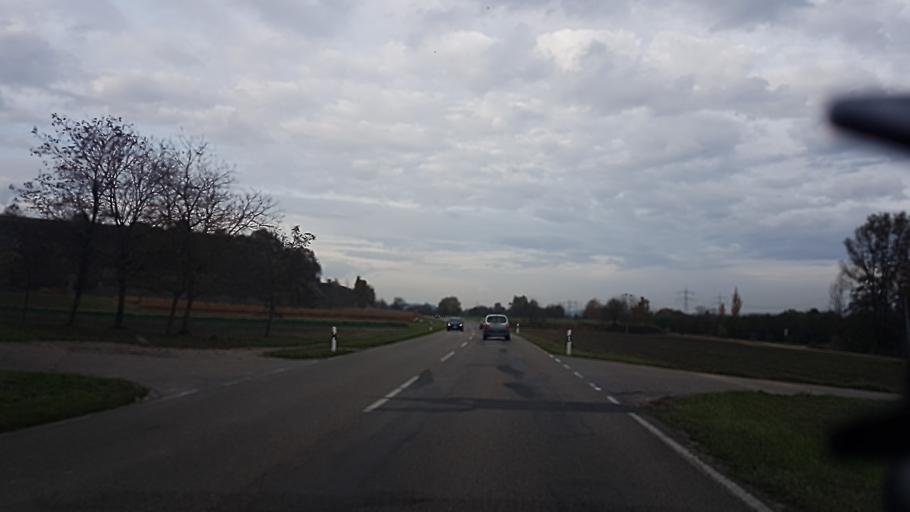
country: DE
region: Baden-Wuerttemberg
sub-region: Freiburg Region
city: Eichstetten
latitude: 48.1061
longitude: 7.7449
